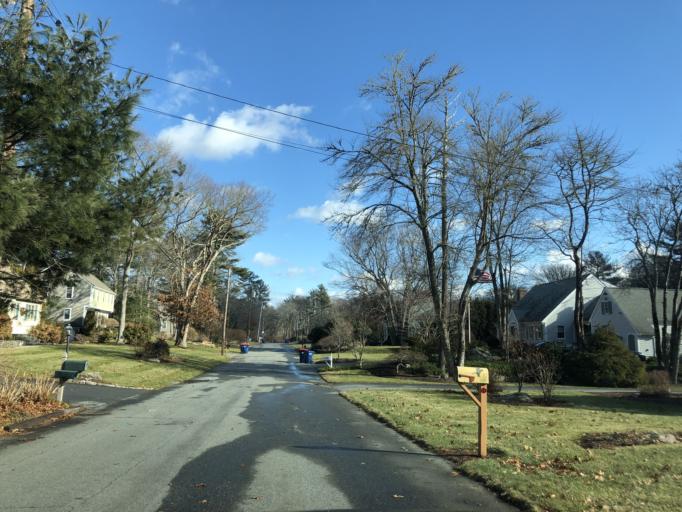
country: US
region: Massachusetts
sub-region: Plymouth County
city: Mattapoisett Center
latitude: 41.6781
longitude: -70.8243
